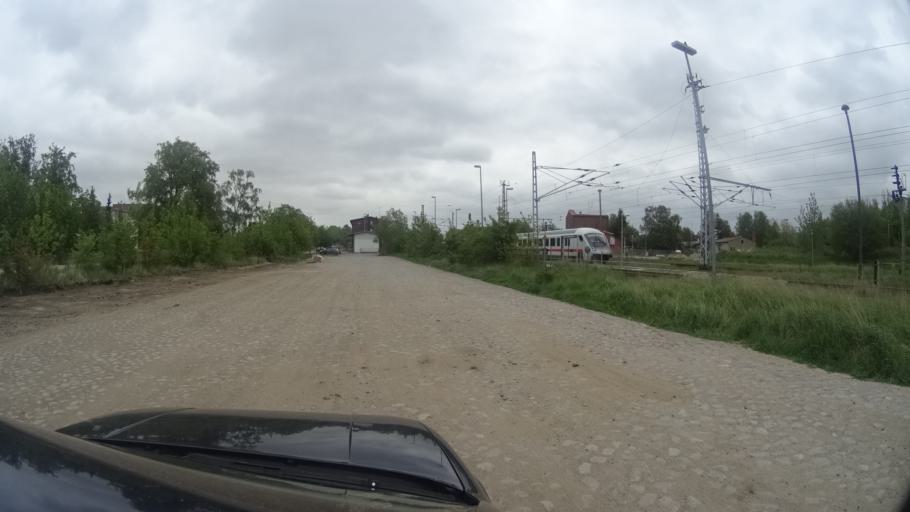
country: DE
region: Mecklenburg-Vorpommern
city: Ribnitz-Damgarten
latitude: 54.2392
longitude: 12.4344
